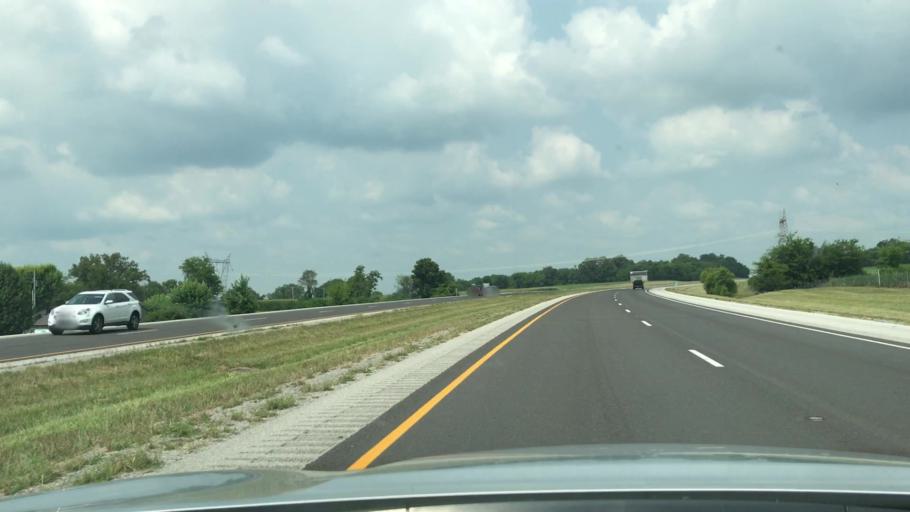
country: US
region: Kentucky
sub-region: Todd County
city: Elkton
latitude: 36.8029
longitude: -87.1001
